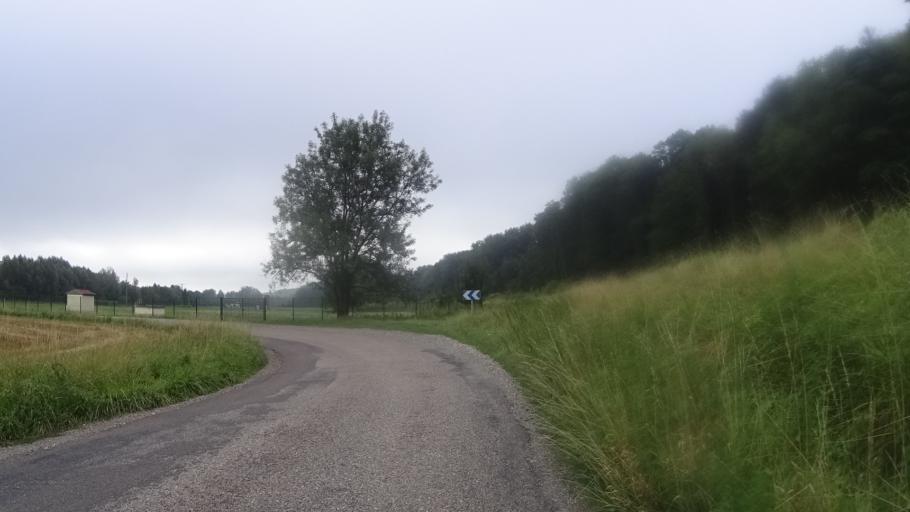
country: FR
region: Lorraine
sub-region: Departement de la Meuse
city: Revigny-sur-Ornain
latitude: 48.8108
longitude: 5.0460
